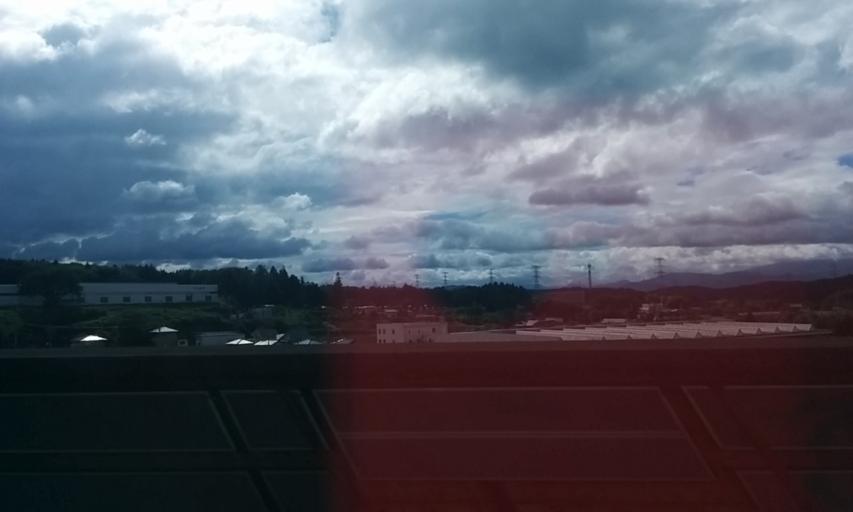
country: JP
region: Tochigi
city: Yaita
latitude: 36.7596
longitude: 139.9431
